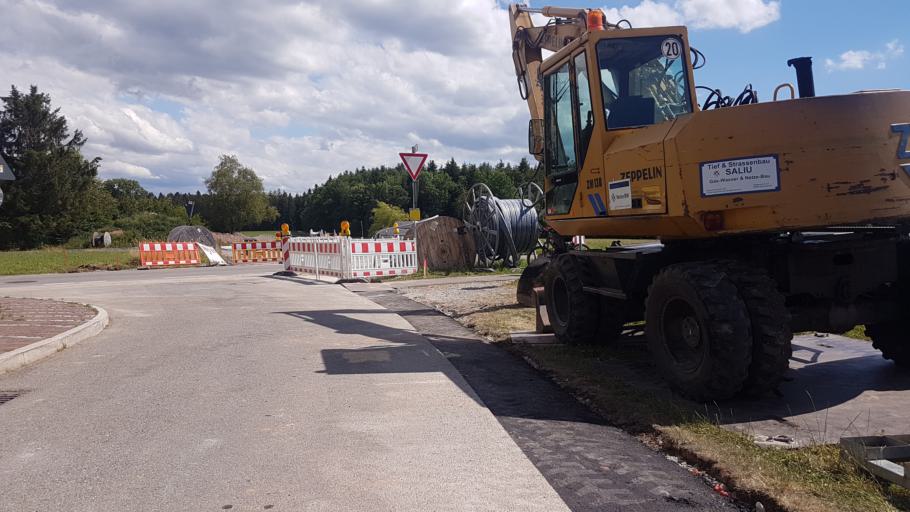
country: DE
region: Baden-Wuerttemberg
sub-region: Freiburg Region
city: Schramberg
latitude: 48.2171
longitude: 8.4171
